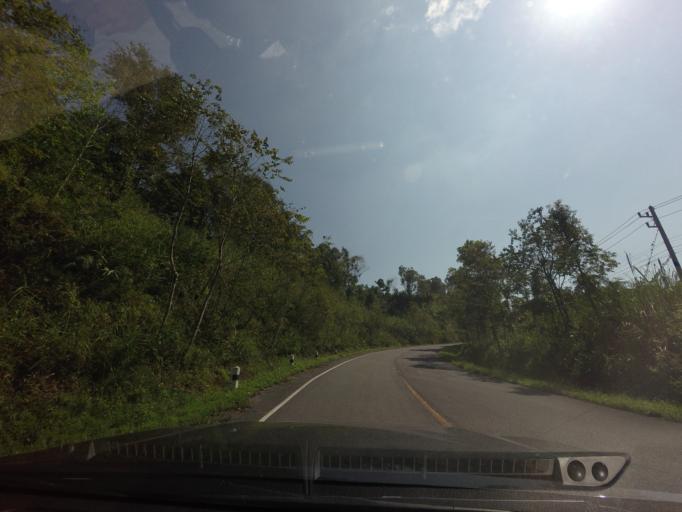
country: TH
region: Nan
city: Bo Kluea
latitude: 19.0473
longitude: 101.0908
